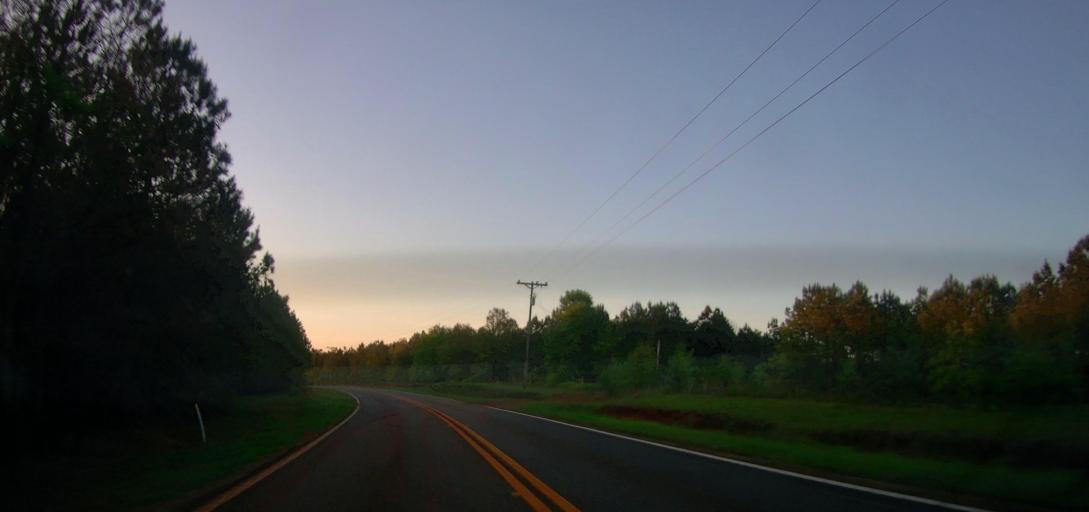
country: US
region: Georgia
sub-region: Marion County
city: Buena Vista
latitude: 32.3884
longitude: -84.5659
